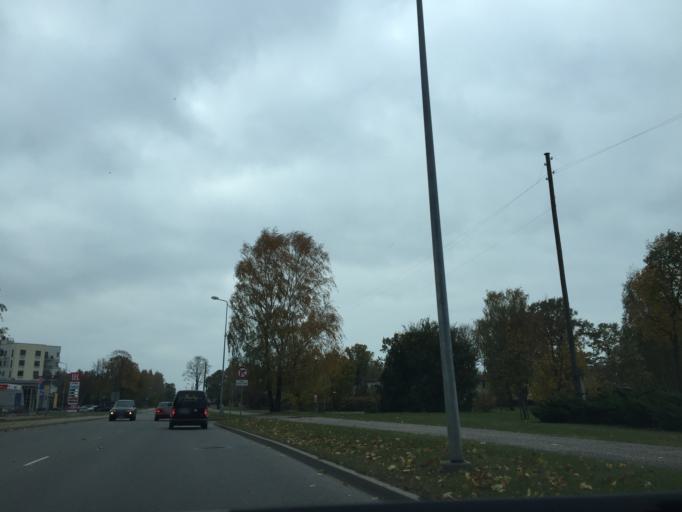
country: LV
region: Riga
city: Riga
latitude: 56.9116
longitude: 24.0959
